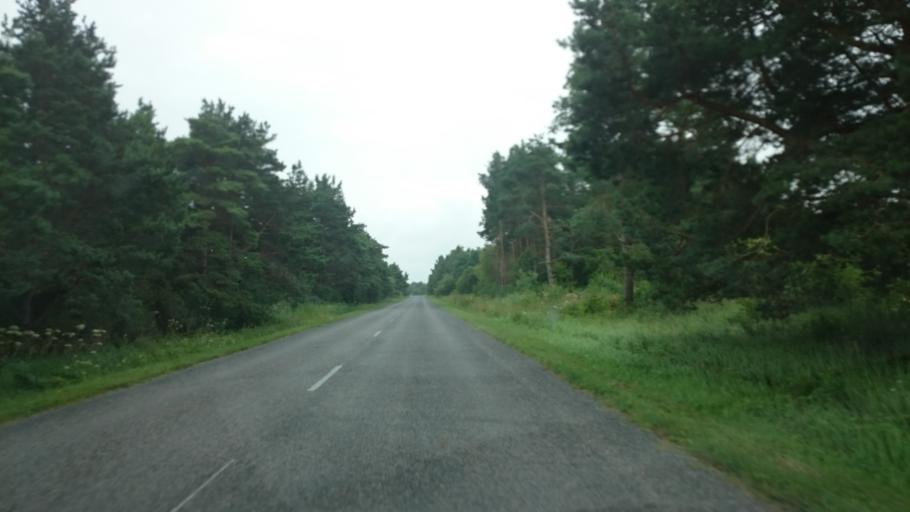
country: EE
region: Saare
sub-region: Orissaare vald
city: Orissaare
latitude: 58.5796
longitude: 23.0276
